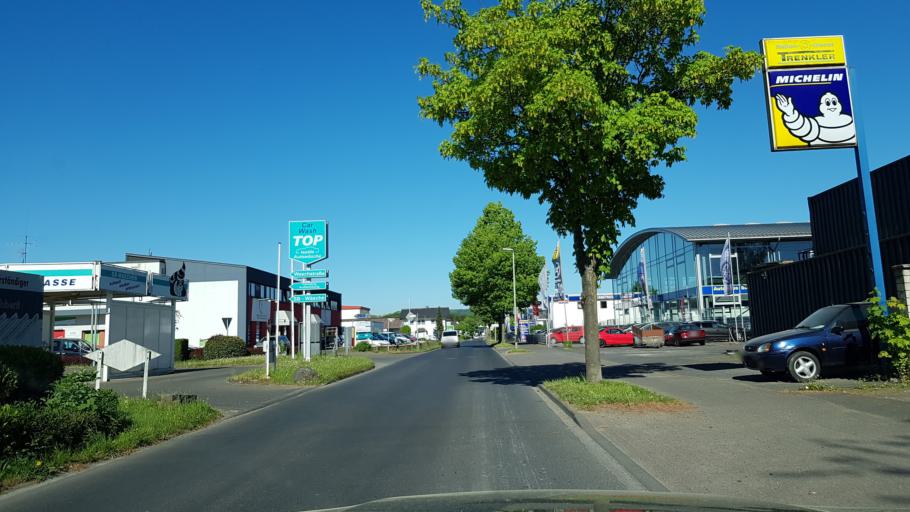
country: DE
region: North Rhine-Westphalia
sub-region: Regierungsbezirk Koln
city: Eitorf
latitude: 50.7710
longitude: 7.4680
